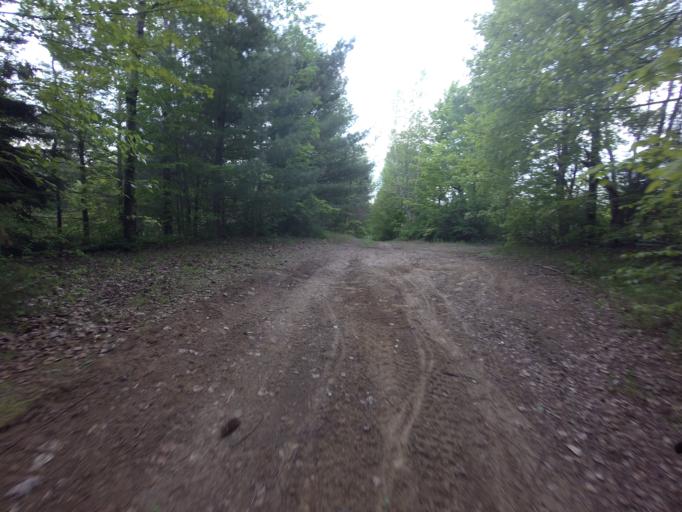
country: US
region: New York
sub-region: St. Lawrence County
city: Gouverneur
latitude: 44.1535
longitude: -75.3285
